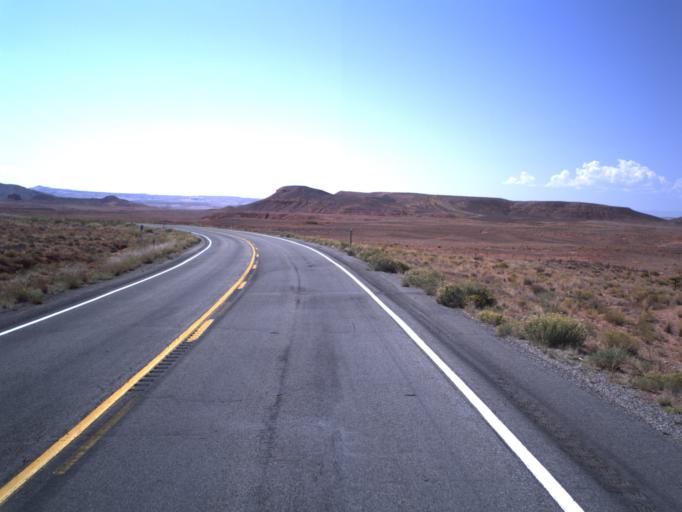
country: US
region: Utah
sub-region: San Juan County
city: Blanding
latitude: 37.0135
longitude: -109.6123
